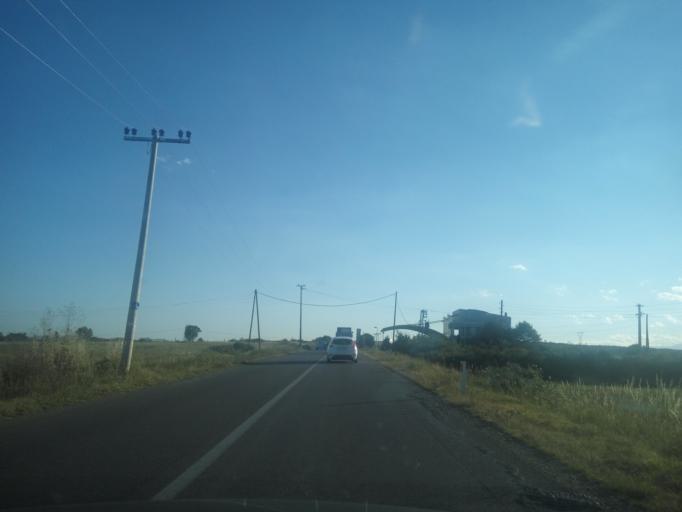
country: XK
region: Gjakova
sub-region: Komuna e Gjakoves
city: Gjakove
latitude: 42.4538
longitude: 20.5026
